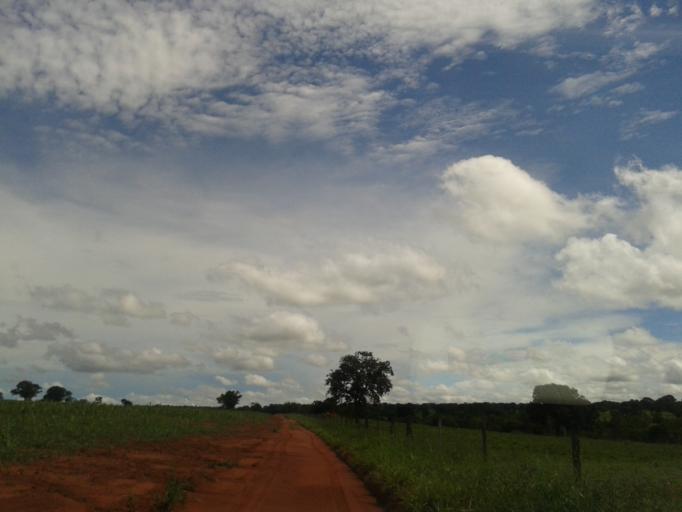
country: BR
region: Minas Gerais
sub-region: Santa Vitoria
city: Santa Vitoria
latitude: -19.1372
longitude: -50.4865
